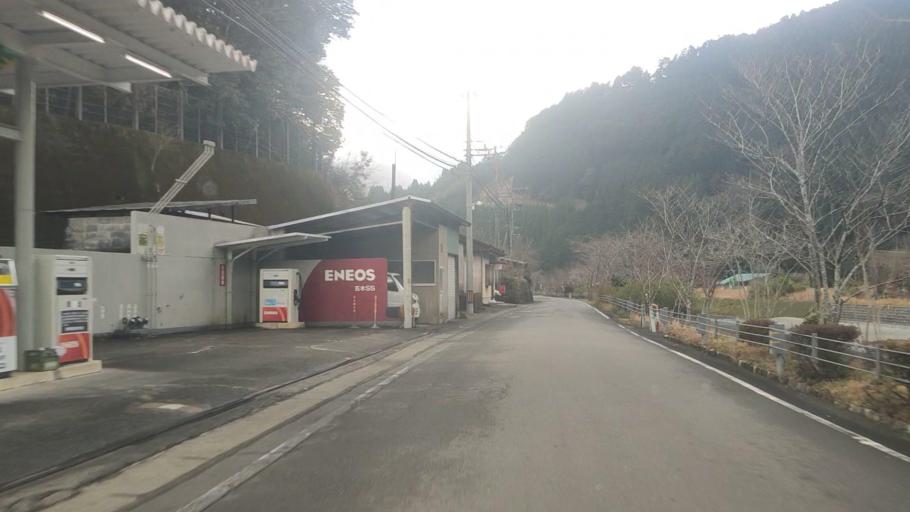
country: JP
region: Kumamoto
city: Hitoyoshi
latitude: 32.4401
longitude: 130.8572
